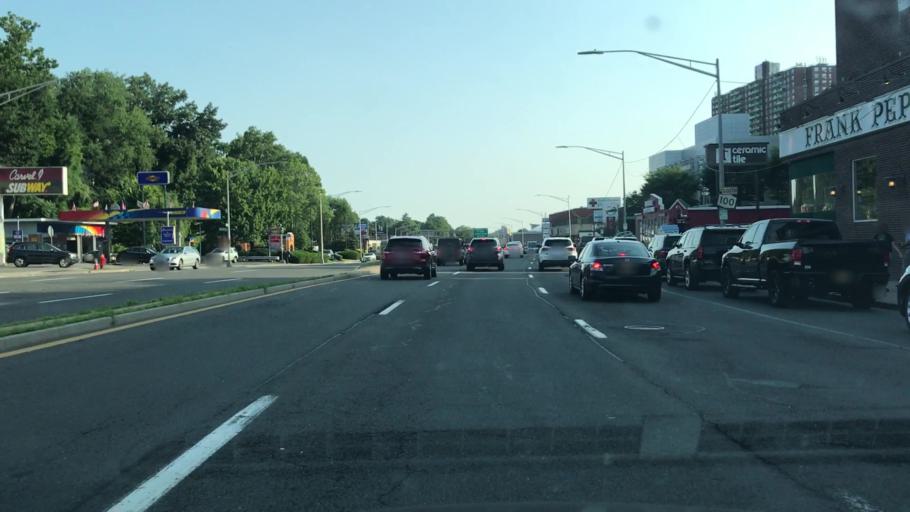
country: US
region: New York
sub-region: Westchester County
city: Tuckahoe
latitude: 40.9654
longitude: -73.8385
